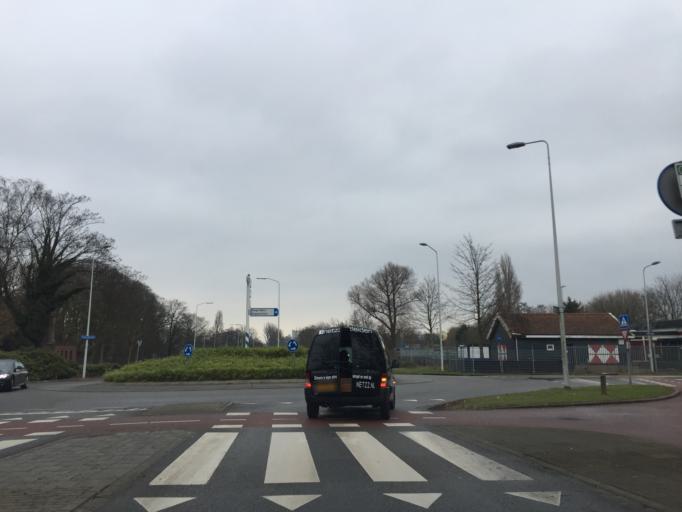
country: NL
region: South Holland
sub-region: Gemeente Oegstgeest
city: Oegstgeest
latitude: 52.1598
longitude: 4.4515
